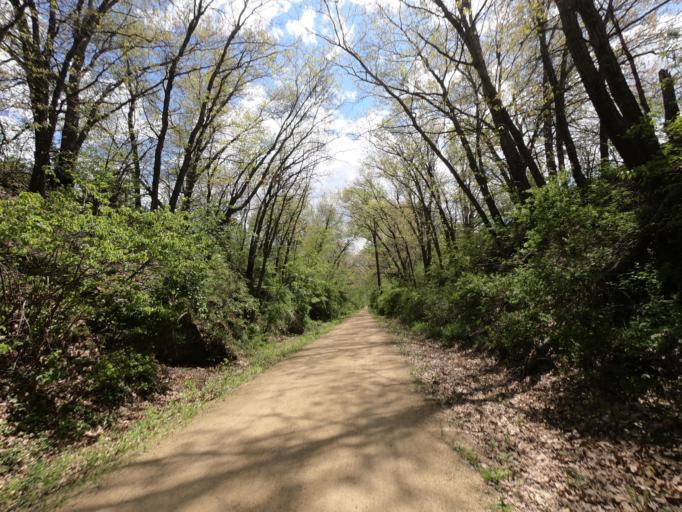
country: US
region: Wisconsin
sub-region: Dane County
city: Fitchburg
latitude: 42.9197
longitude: -89.5108
